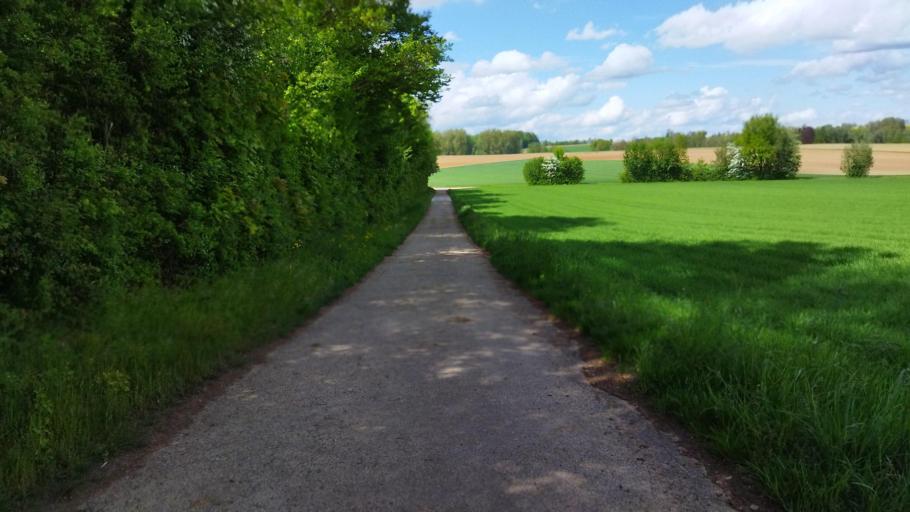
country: DE
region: Baden-Wuerttemberg
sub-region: Regierungsbezirk Stuttgart
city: Bad Rappenau
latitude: 49.2202
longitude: 9.0902
